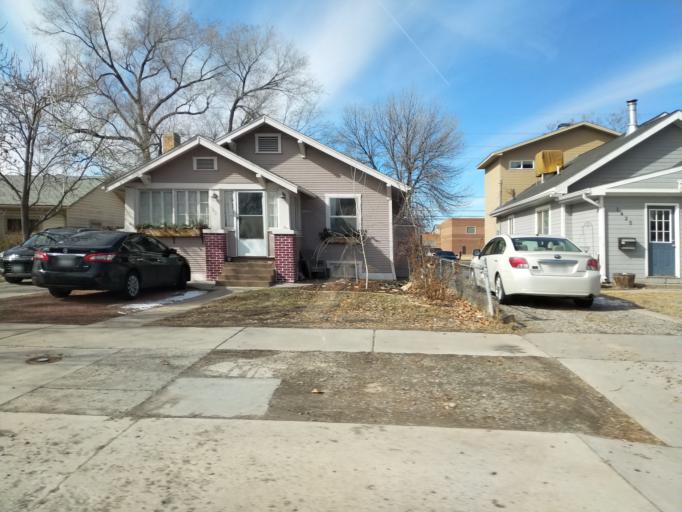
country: US
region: Colorado
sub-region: Mesa County
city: Grand Junction
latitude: 39.0805
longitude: -108.5611
